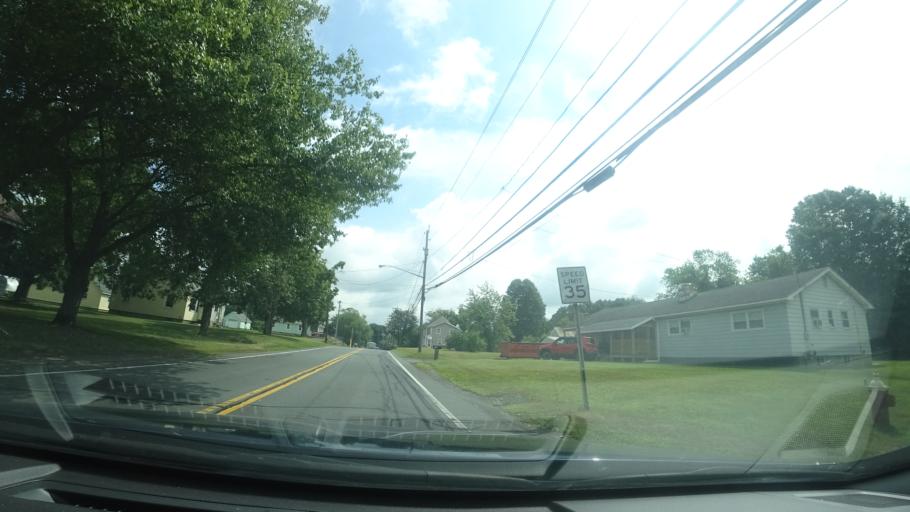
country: US
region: New York
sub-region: Washington County
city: Hudson Falls
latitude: 43.3165
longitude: -73.6004
